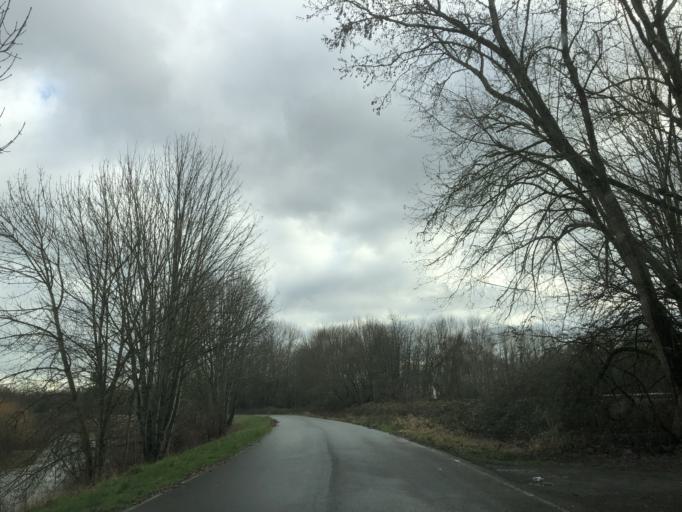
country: US
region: Washington
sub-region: King County
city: Kent
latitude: 47.3770
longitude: -122.2683
